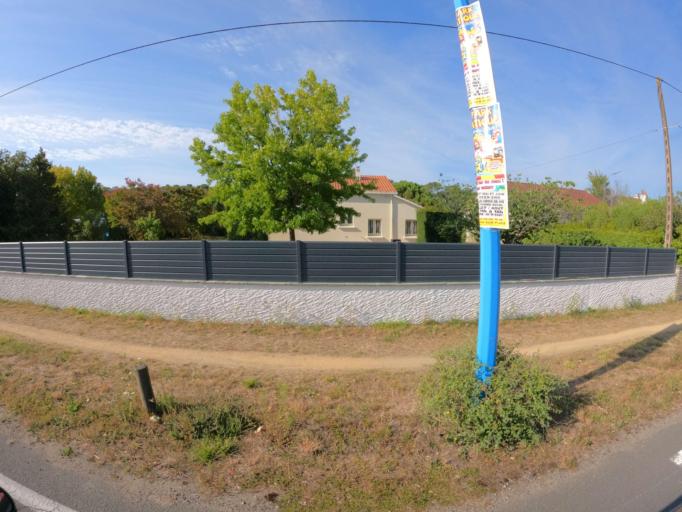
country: FR
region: Pays de la Loire
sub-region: Departement de la Vendee
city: Saint-Jean-de-Monts
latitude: 46.8049
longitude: -2.0941
